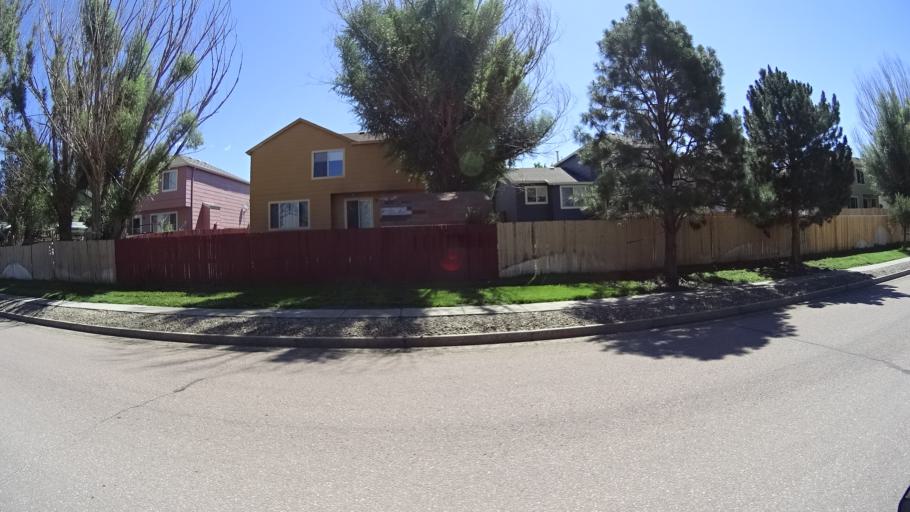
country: US
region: Colorado
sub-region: El Paso County
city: Security-Widefield
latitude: 38.7662
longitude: -104.6551
